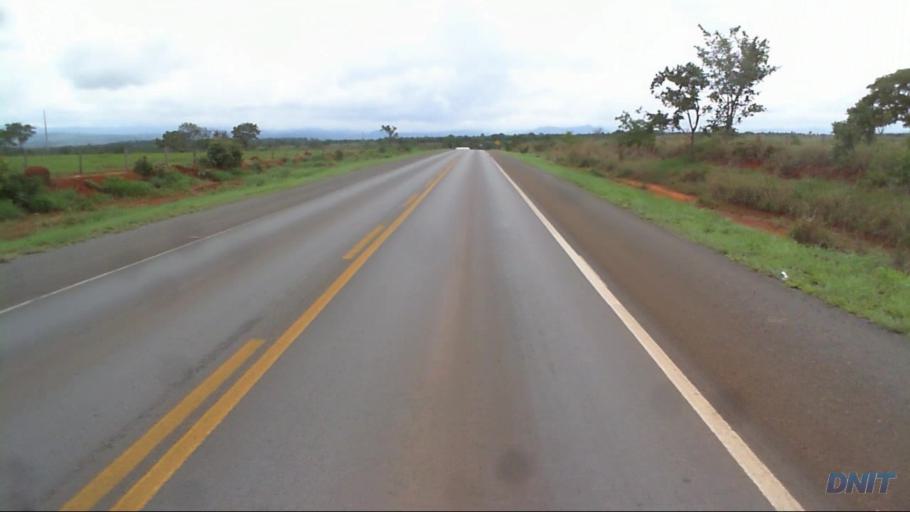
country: BR
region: Goias
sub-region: Padre Bernardo
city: Padre Bernardo
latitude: -15.1590
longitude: -48.3578
